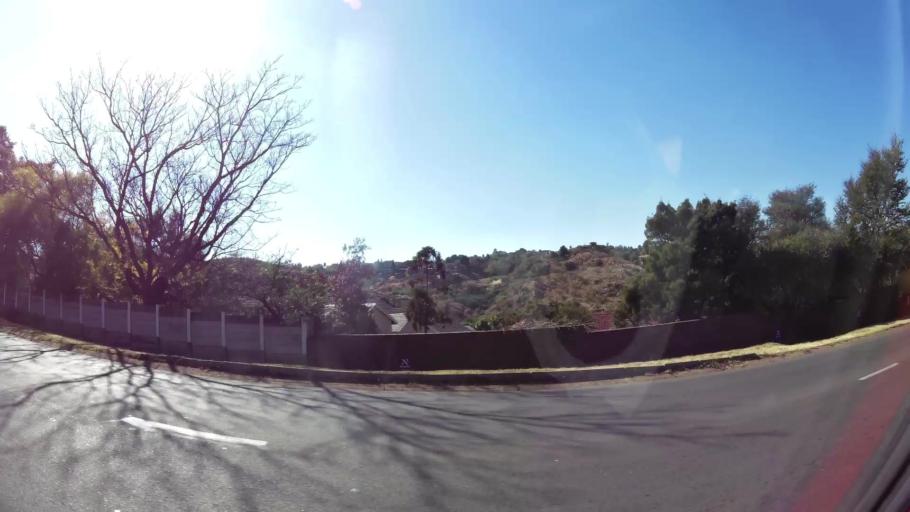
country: ZA
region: Gauteng
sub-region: City of Johannesburg Metropolitan Municipality
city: Roodepoort
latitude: -26.1386
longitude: 27.8917
